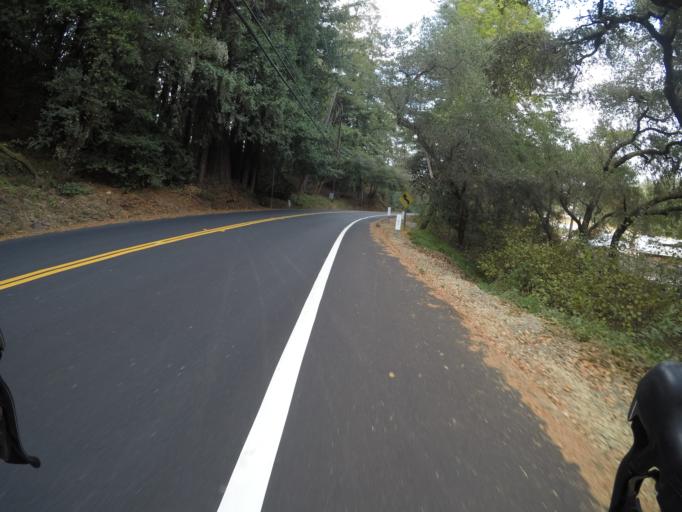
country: US
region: California
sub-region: Santa Cruz County
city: Scotts Valley
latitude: 37.0798
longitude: -122.0042
